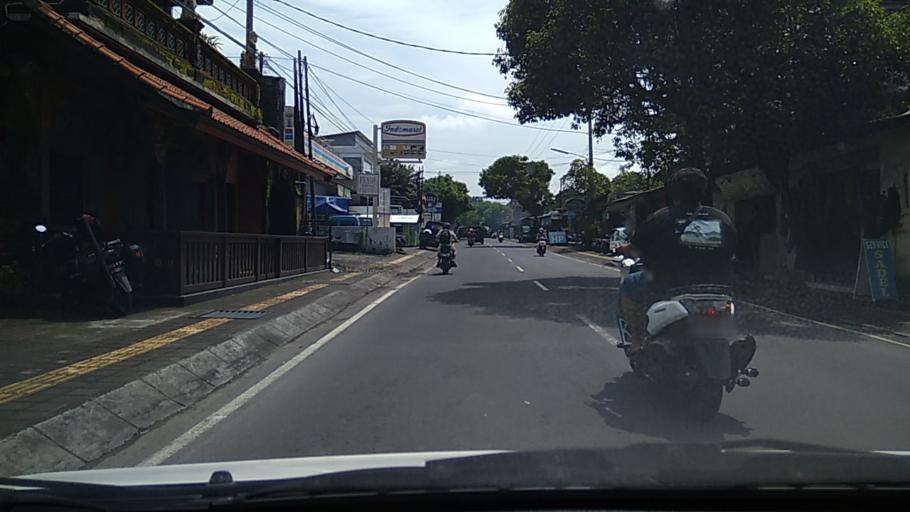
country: ID
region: Bali
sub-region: Kabupaten Gianyar
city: Ubud
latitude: -8.5239
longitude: 115.2728
